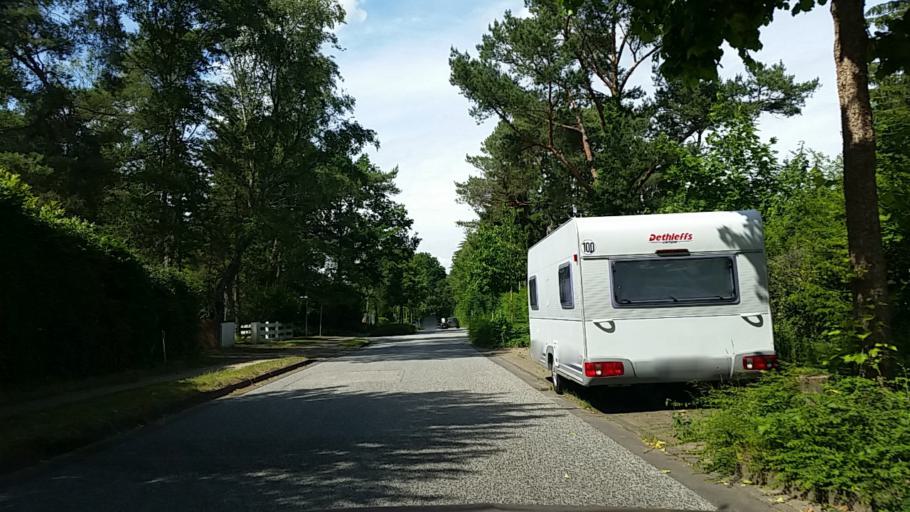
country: DE
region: Schleswig-Holstein
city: Wedel
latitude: 53.5873
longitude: 9.7639
